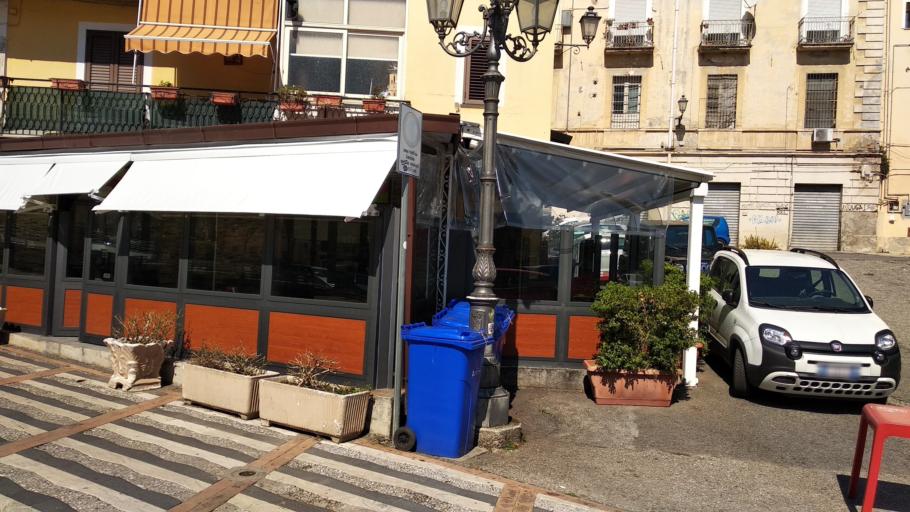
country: IT
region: Calabria
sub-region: Provincia di Catanzaro
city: Lamezia Terme
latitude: 38.9751
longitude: 16.3200
